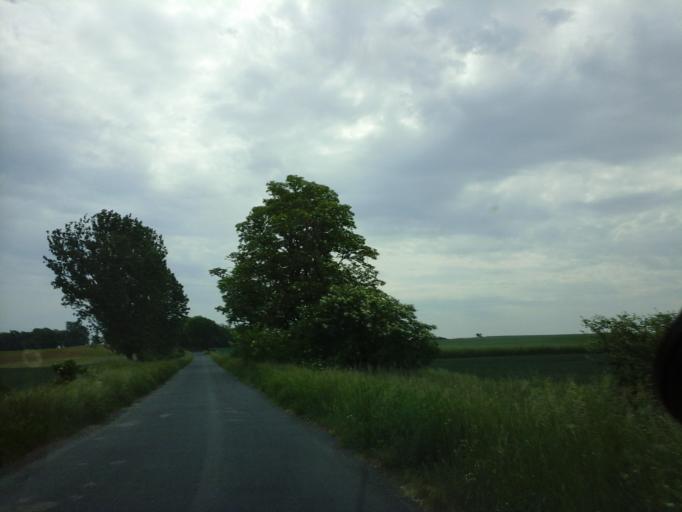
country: PL
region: West Pomeranian Voivodeship
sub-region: Powiat choszczenski
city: Krzecin
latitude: 53.1567
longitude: 15.5173
